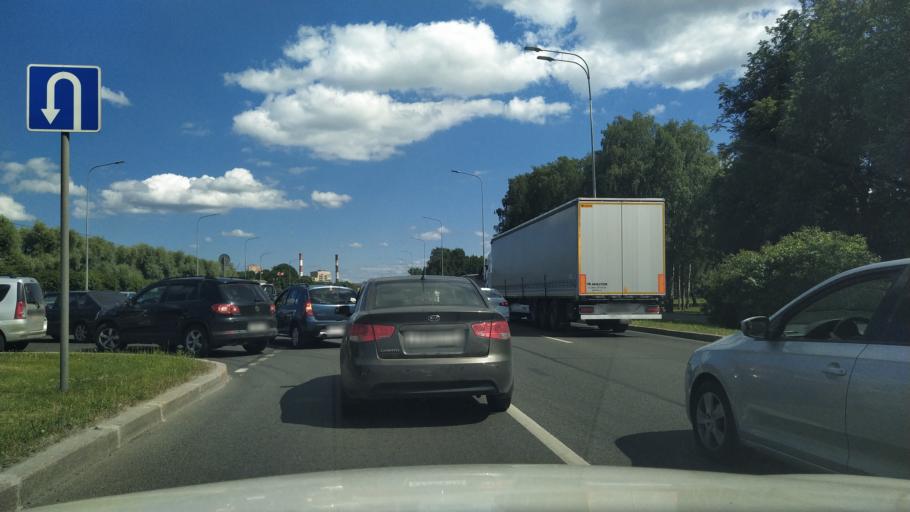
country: RU
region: Leningrad
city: Kalininskiy
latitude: 59.9943
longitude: 30.4159
